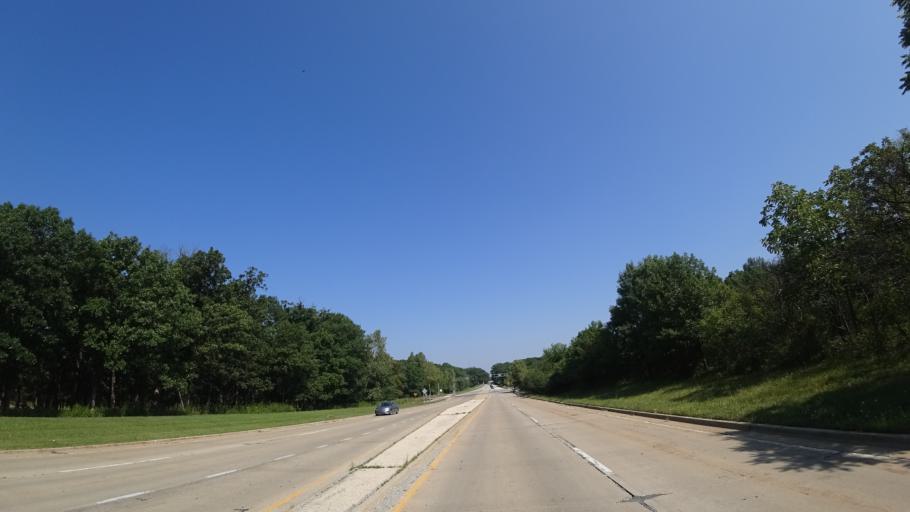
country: US
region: Illinois
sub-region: Cook County
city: Oak Forest
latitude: 41.5889
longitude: -87.7555
